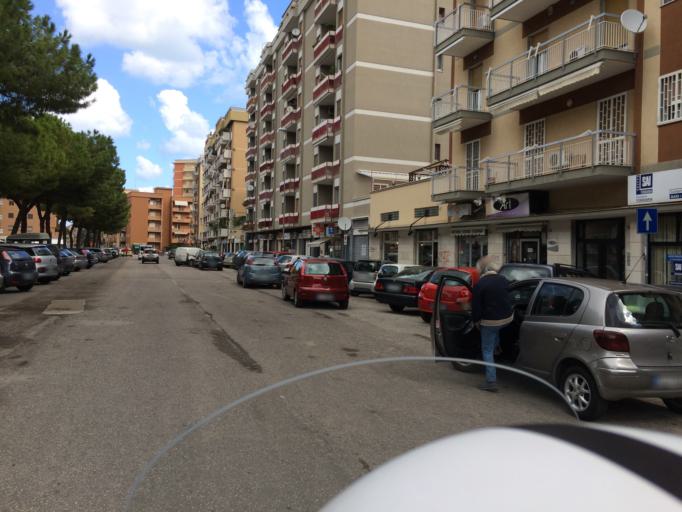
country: IT
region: Apulia
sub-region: Provincia di Bari
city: Bari
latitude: 41.1030
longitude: 16.8778
